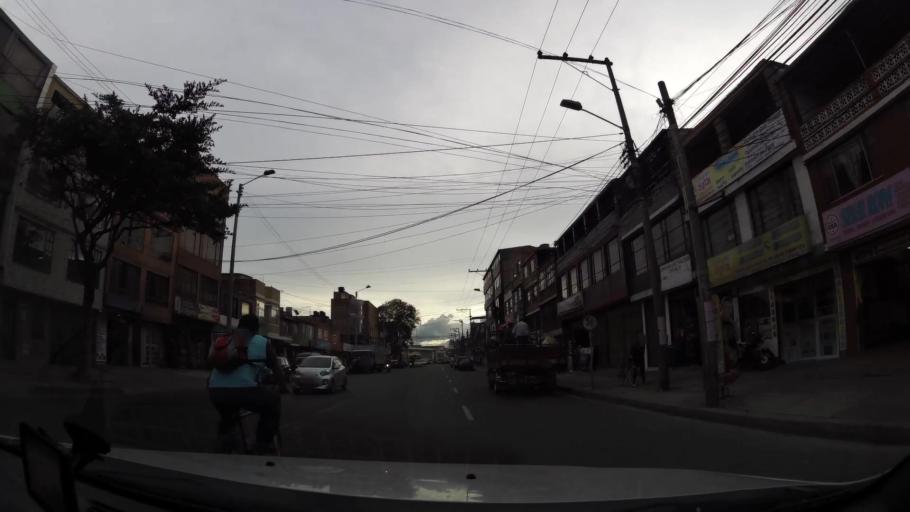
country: CO
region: Cundinamarca
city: Soacha
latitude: 4.6218
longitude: -74.1589
